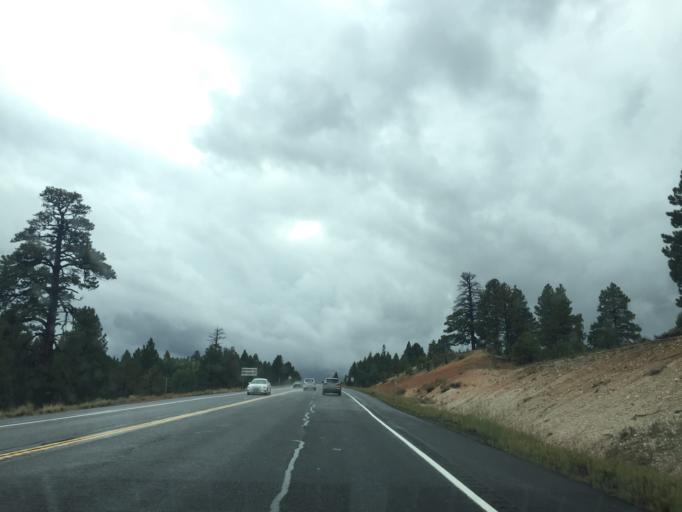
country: US
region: Utah
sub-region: Garfield County
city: Panguitch
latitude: 37.4941
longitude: -112.5093
